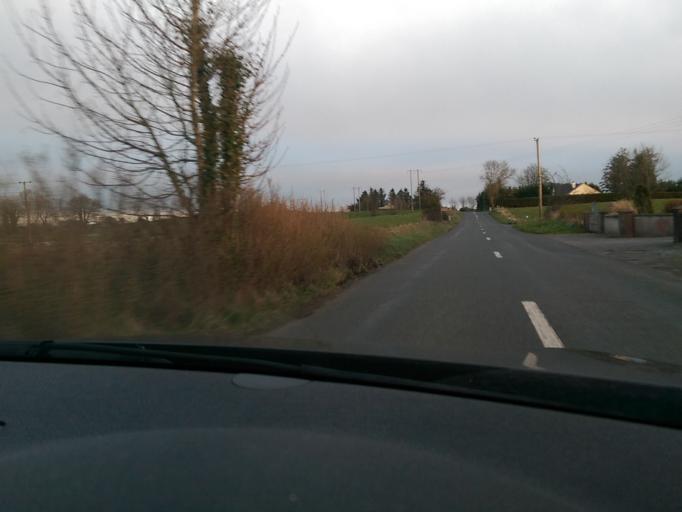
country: IE
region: Connaught
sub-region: Sligo
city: Ballymote
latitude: 54.0216
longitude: -8.5646
